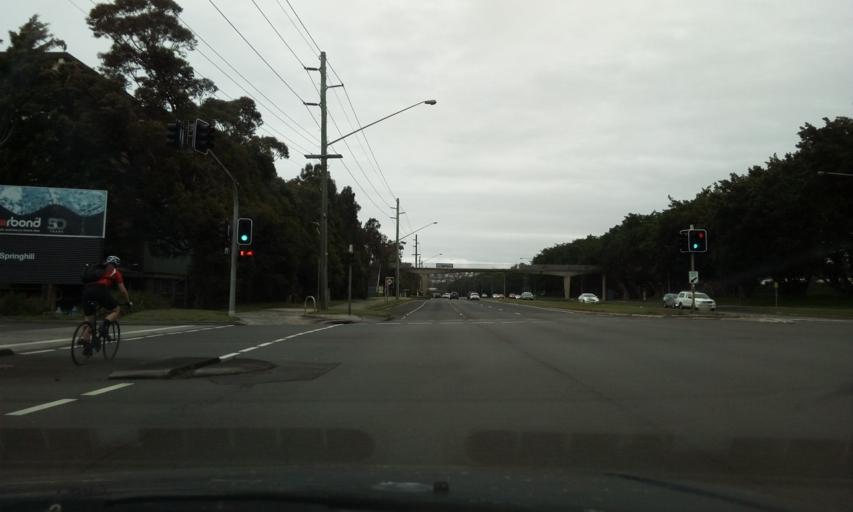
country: AU
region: New South Wales
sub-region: Wollongong
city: Coniston
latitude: -34.4548
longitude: 150.8738
